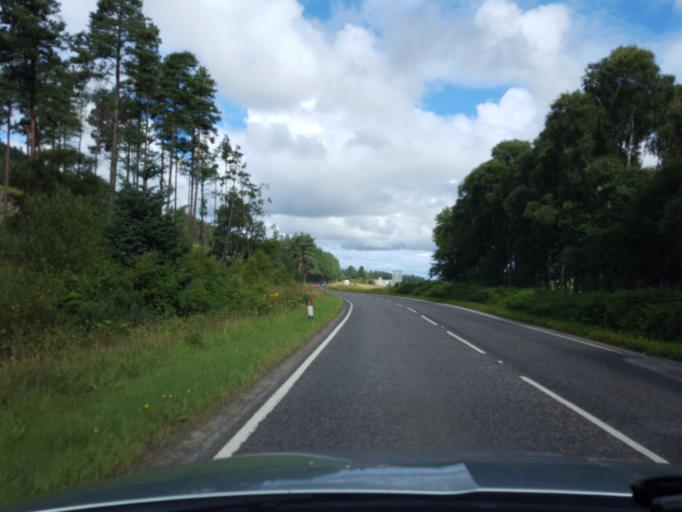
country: GB
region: Scotland
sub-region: Moray
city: Rothes
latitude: 57.5654
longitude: -3.2531
